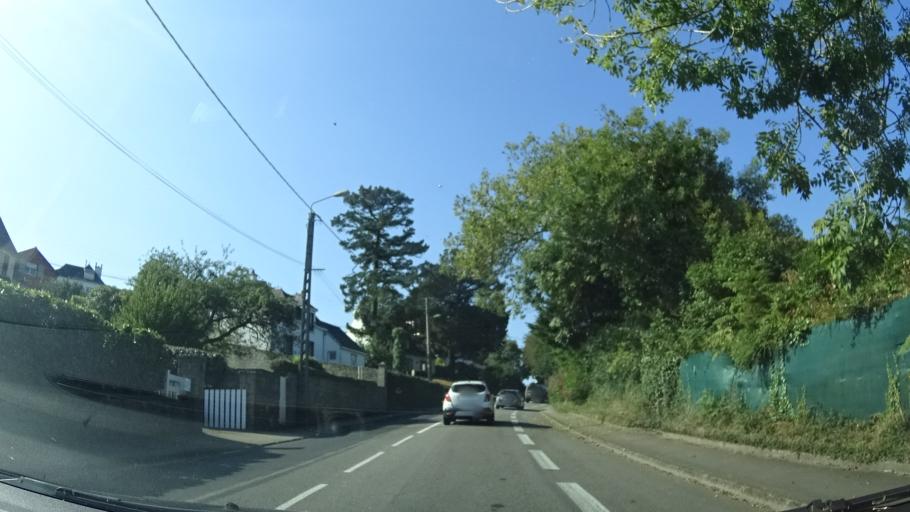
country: FR
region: Brittany
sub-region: Departement du Finistere
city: Douarnenez
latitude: 48.0880
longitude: -4.3049
